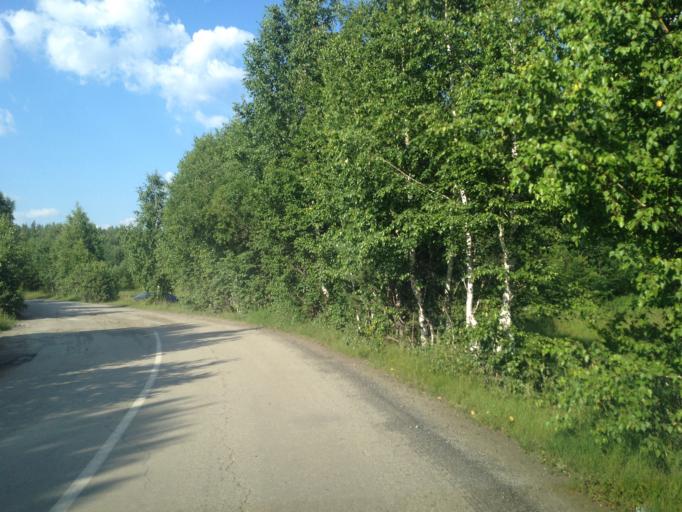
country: RU
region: Chelyabinsk
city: Snezhinsk
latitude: 56.1770
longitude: 60.5687
